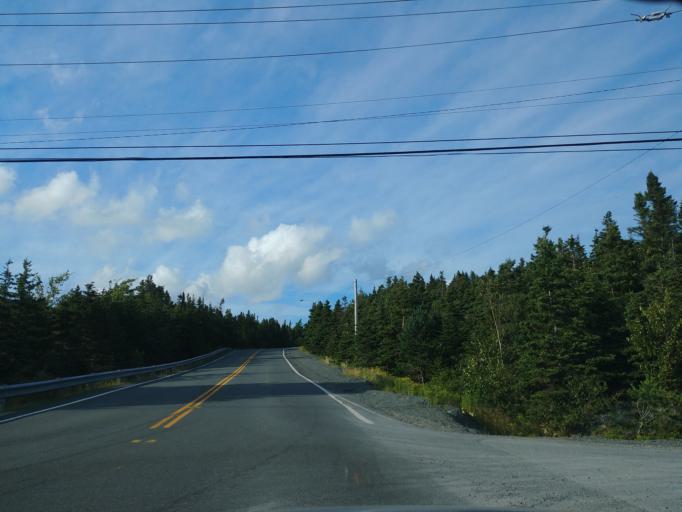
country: CA
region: Newfoundland and Labrador
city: St. John's
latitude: 47.5666
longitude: -52.7623
